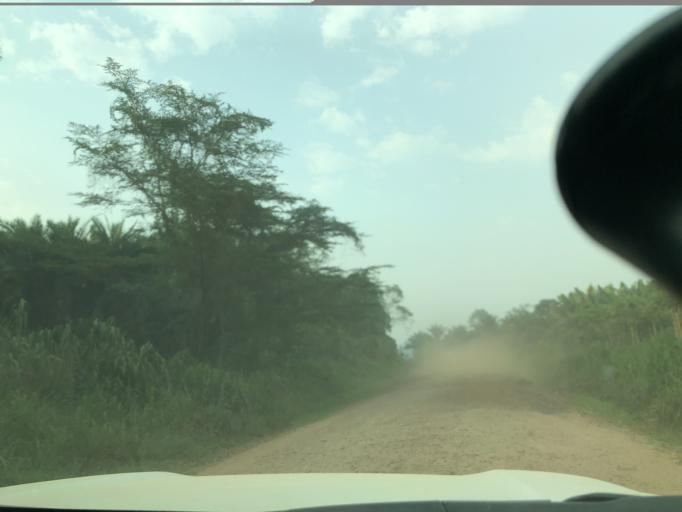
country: UG
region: Western Region
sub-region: Kasese District
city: Margherita
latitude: 0.2807
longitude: 29.6696
